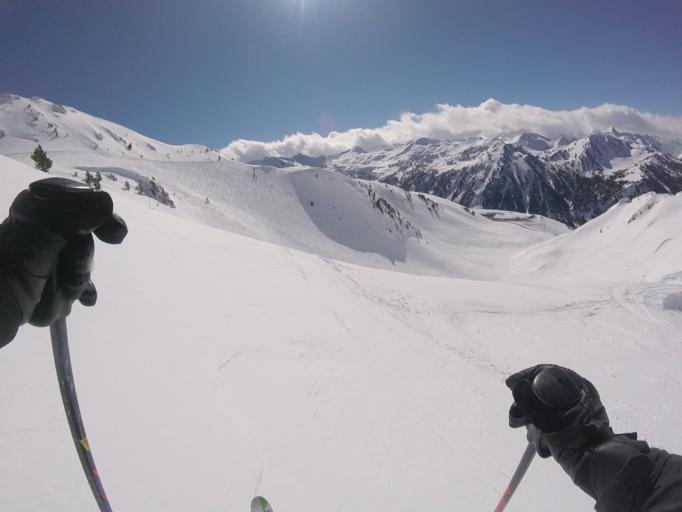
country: ES
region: Catalonia
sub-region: Provincia de Lleida
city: Espot
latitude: 42.6718
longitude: 0.9872
